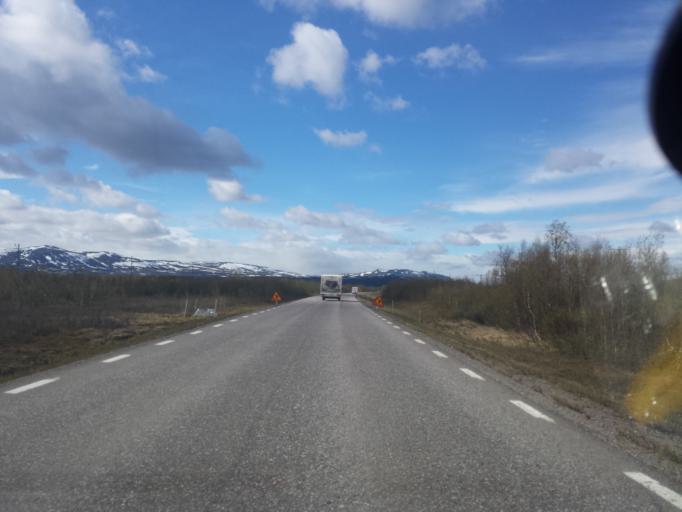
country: SE
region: Norrbotten
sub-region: Kiruna Kommun
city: Kiruna
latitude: 68.0032
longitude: 19.8554
